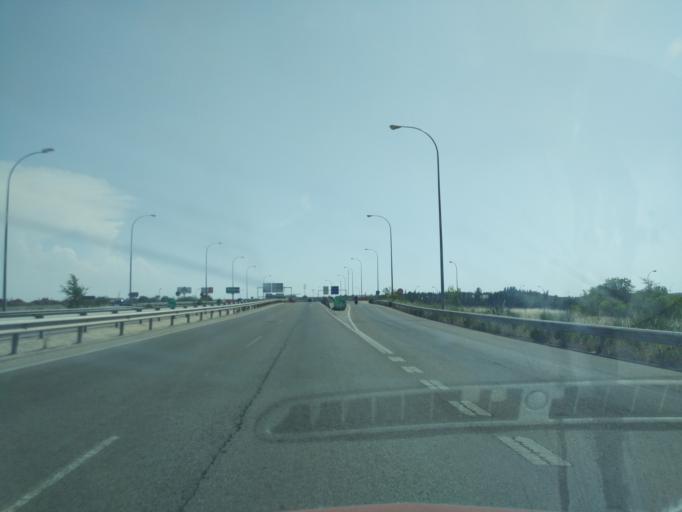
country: ES
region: Madrid
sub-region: Provincia de Madrid
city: Leganes
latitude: 40.3541
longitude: -3.7505
